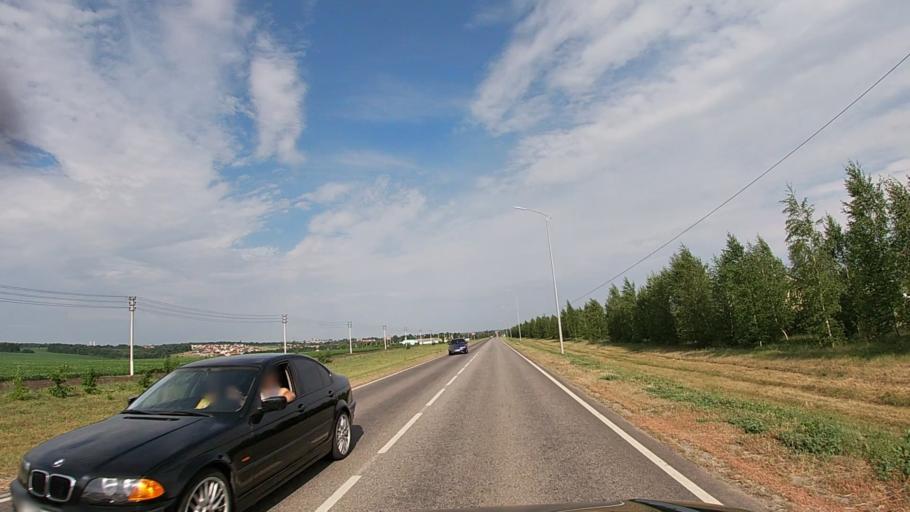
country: RU
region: Belgorod
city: Krasnaya Yaruga
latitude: 50.7971
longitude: 35.6882
